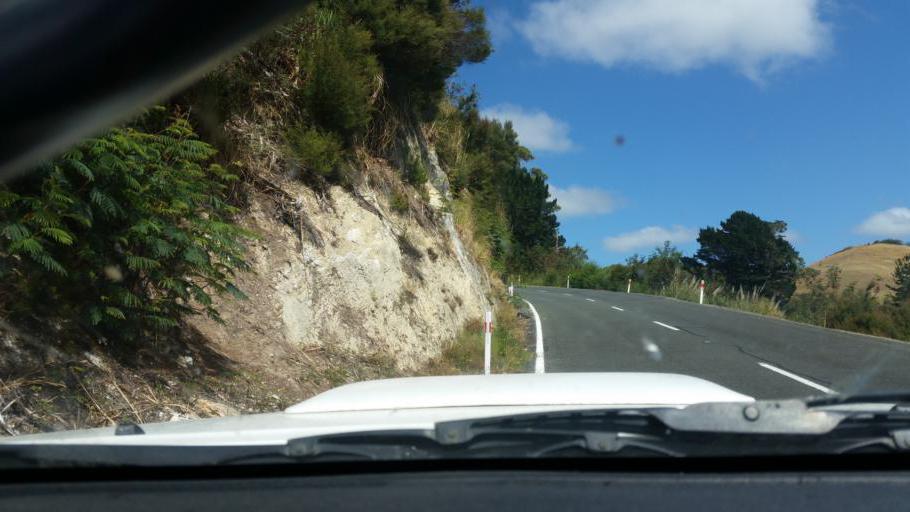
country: NZ
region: Northland
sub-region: Kaipara District
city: Dargaville
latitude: -35.8227
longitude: 173.6934
